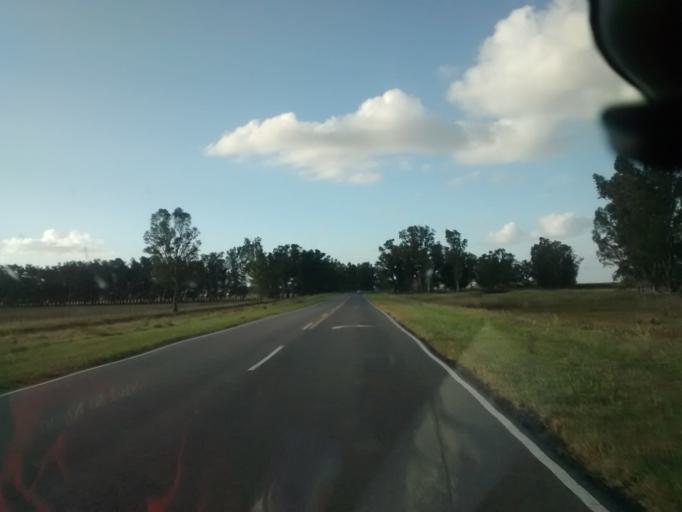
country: AR
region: Buenos Aires
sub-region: Partido de General Belgrano
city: General Belgrano
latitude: -36.1491
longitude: -58.5953
